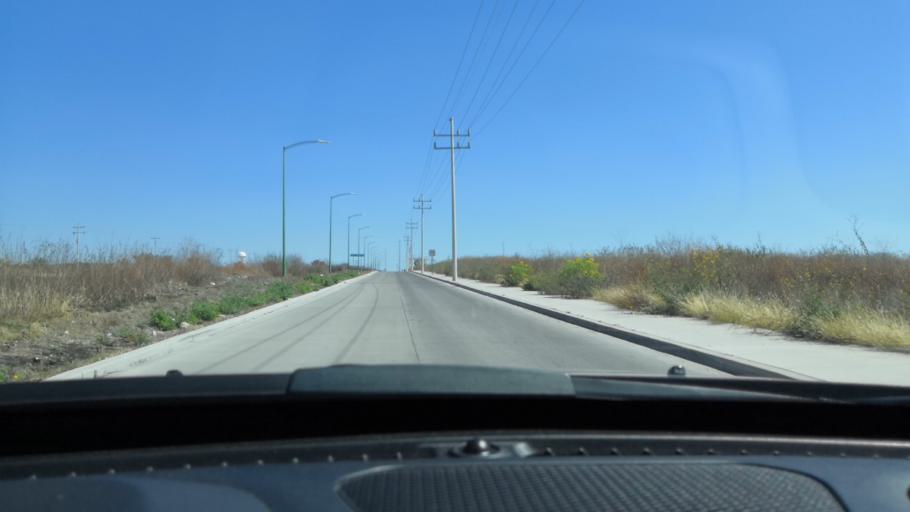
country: MX
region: Guanajuato
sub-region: Leon
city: Centro Familiar la Soledad
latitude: 21.1073
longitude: -101.7629
